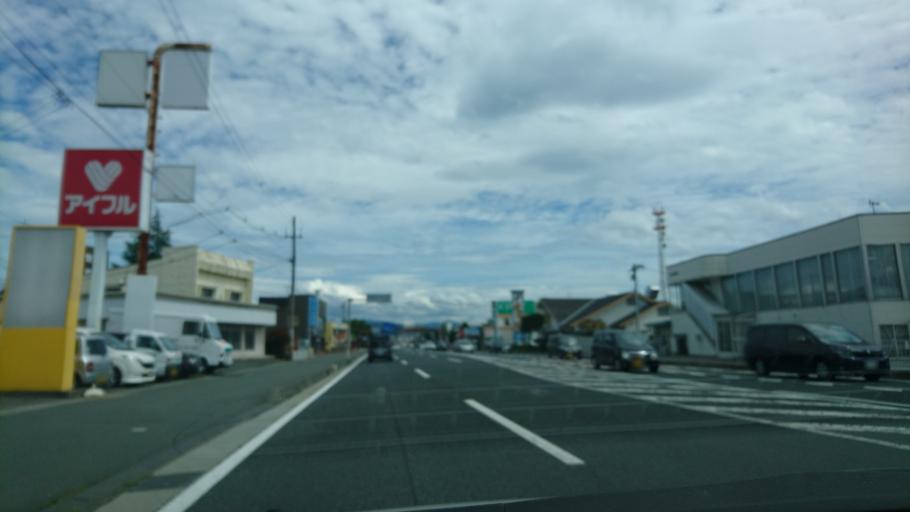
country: JP
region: Iwate
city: Morioka-shi
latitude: 39.7220
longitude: 141.1370
